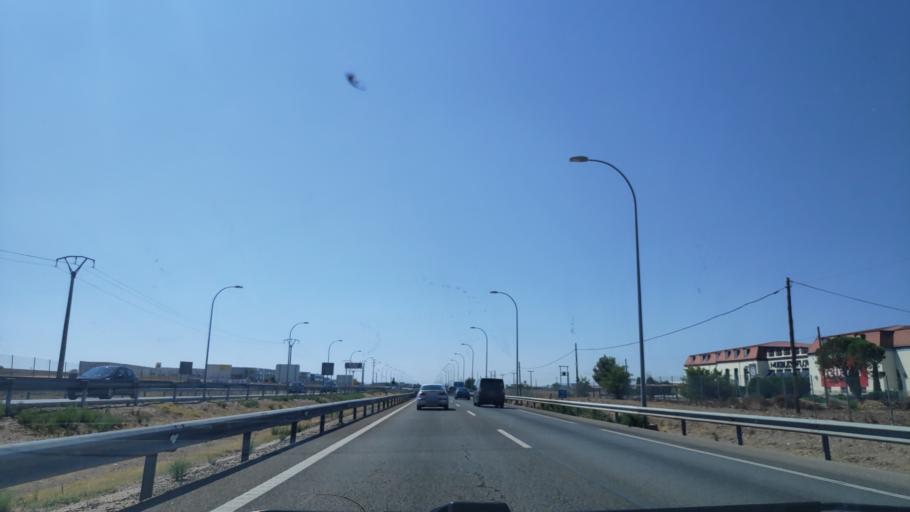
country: ES
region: Madrid
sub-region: Provincia de Madrid
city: Torrejon de la Calzada
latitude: 40.1831
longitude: -3.8079
